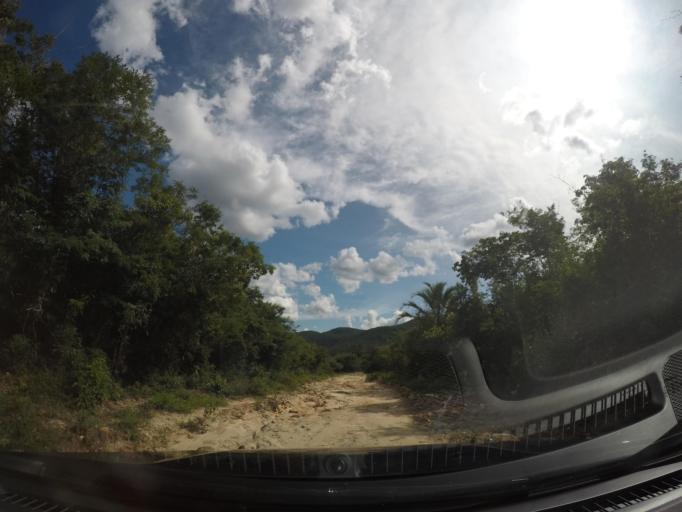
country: BR
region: Bahia
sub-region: Barra Da Estiva
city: Barra da Estiva
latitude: -13.1421
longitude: -41.5927
